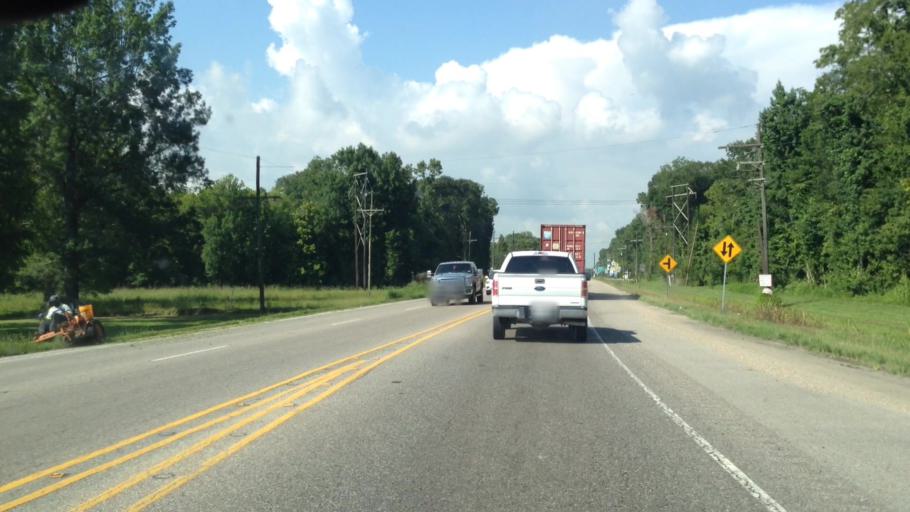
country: US
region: Louisiana
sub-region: Ascension Parish
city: Sorrento
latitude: 30.1693
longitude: -90.8789
